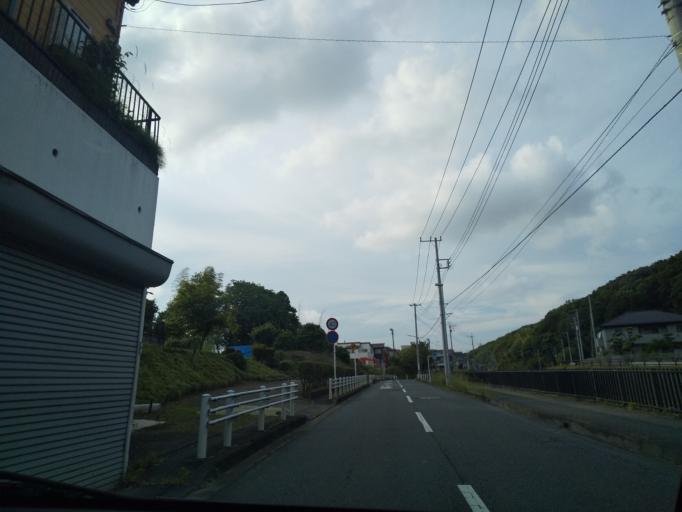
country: JP
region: Kanagawa
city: Zama
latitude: 35.5209
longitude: 139.3845
